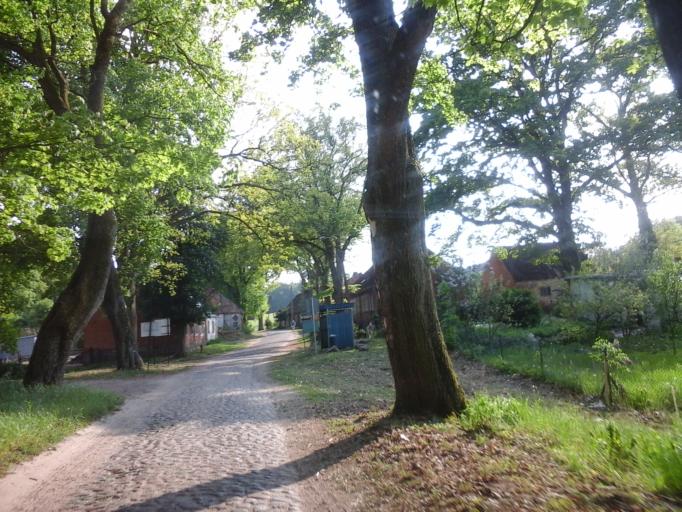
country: PL
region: West Pomeranian Voivodeship
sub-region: Powiat mysliborski
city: Barlinek
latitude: 53.0277
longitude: 15.2265
